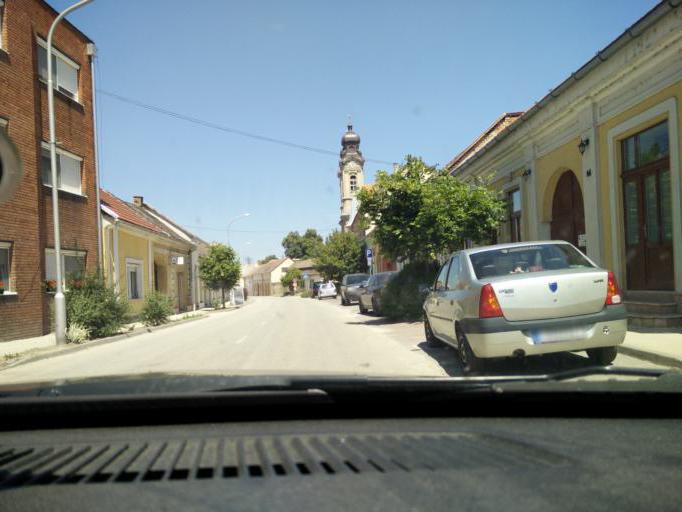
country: HU
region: Komarom-Esztergom
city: Tata
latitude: 47.6415
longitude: 18.3129
